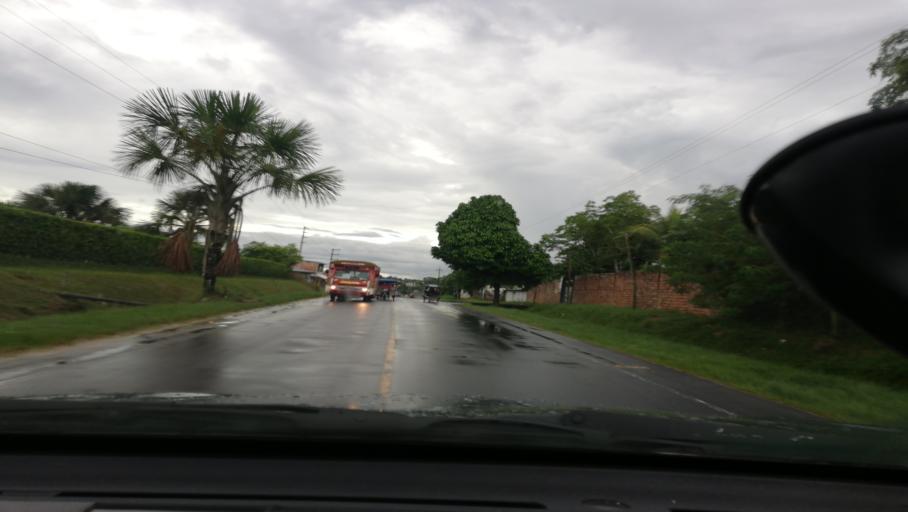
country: PE
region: Loreto
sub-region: Provincia de Maynas
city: Iquitos
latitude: -3.8431
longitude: -73.3349
